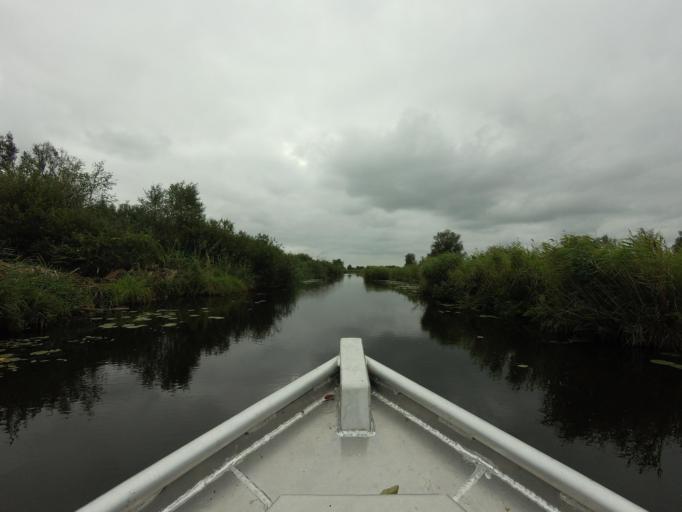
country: NL
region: Overijssel
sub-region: Gemeente Steenwijkerland
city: Oldemarkt
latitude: 52.7973
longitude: 5.9028
